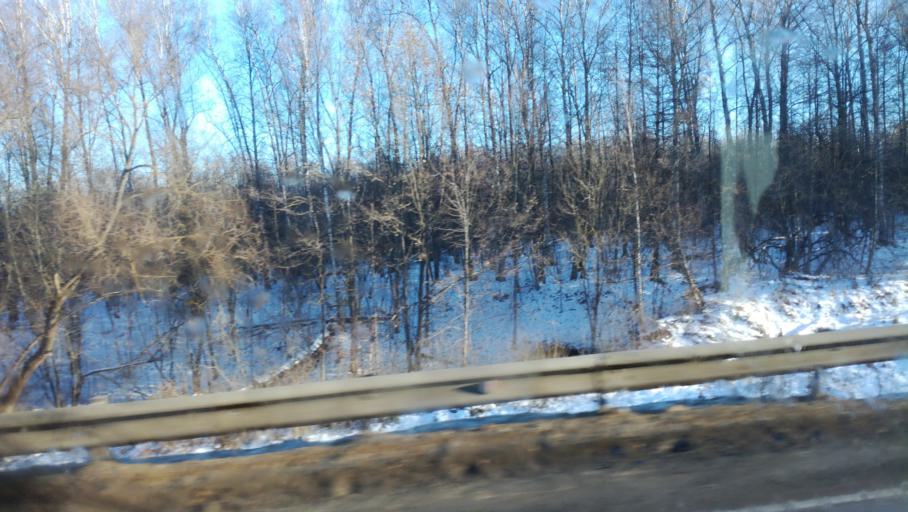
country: RU
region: Tula
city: Kosaya Gora
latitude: 54.1658
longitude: 37.4622
